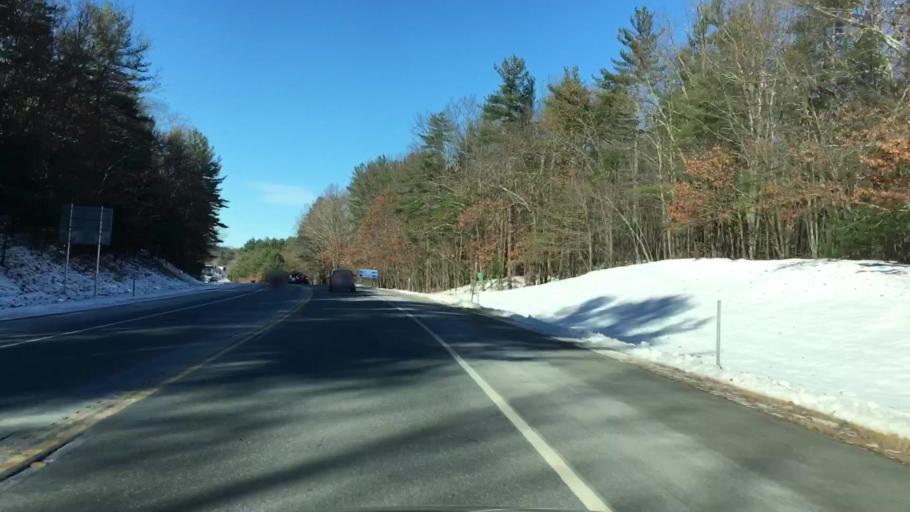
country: US
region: New Hampshire
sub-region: Hillsborough County
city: Milford
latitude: 42.8553
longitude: -71.6105
